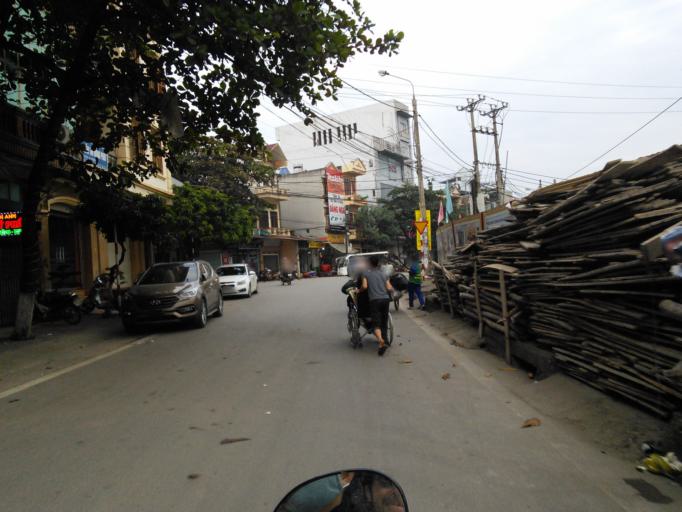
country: VN
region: Lao Cai
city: Lao Cai
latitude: 22.4944
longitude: 103.9756
